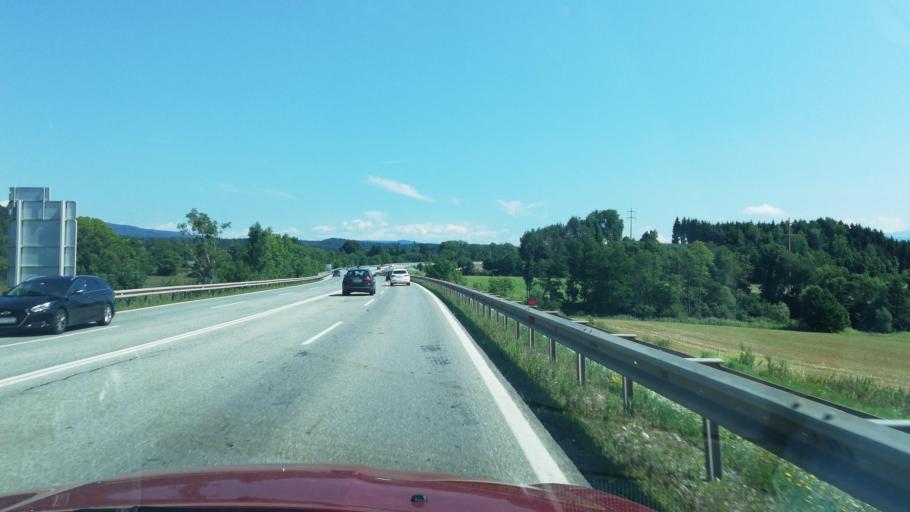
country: AT
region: Carinthia
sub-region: Politischer Bezirk Sankt Veit an der Glan
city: Sankt Veit an der Glan
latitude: 46.7950
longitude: 14.3906
